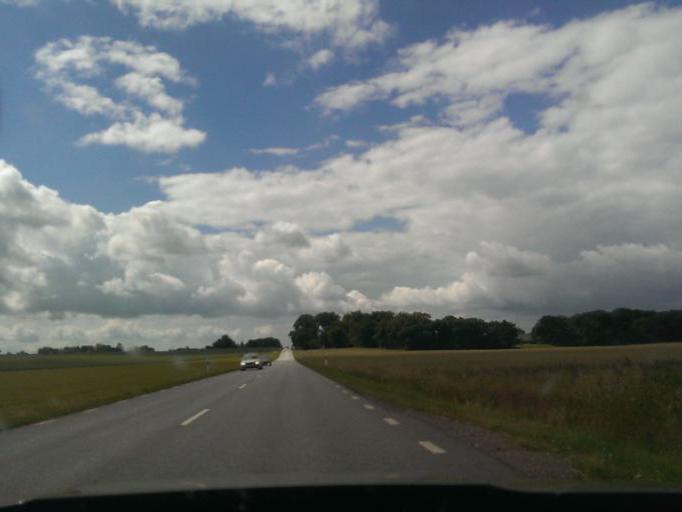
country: SE
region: Skane
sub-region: Eslovs Kommun
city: Eslov
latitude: 55.8787
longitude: 13.3178
